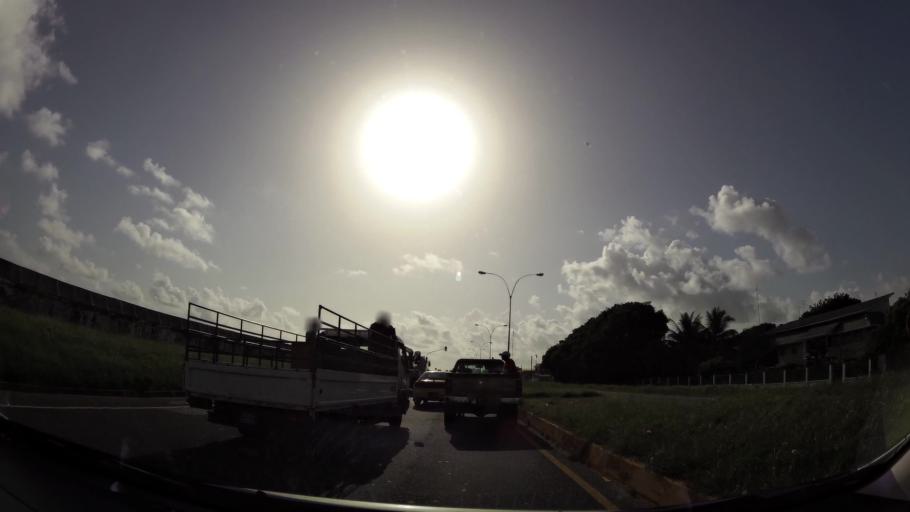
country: GY
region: Demerara-Mahaica
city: Georgetown
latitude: 6.8257
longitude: -58.1307
